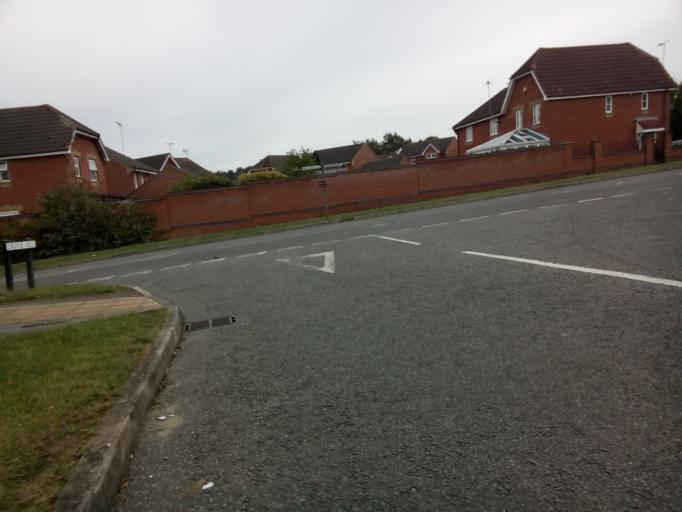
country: GB
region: England
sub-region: Suffolk
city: Ipswich
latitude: 52.0342
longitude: 1.1179
